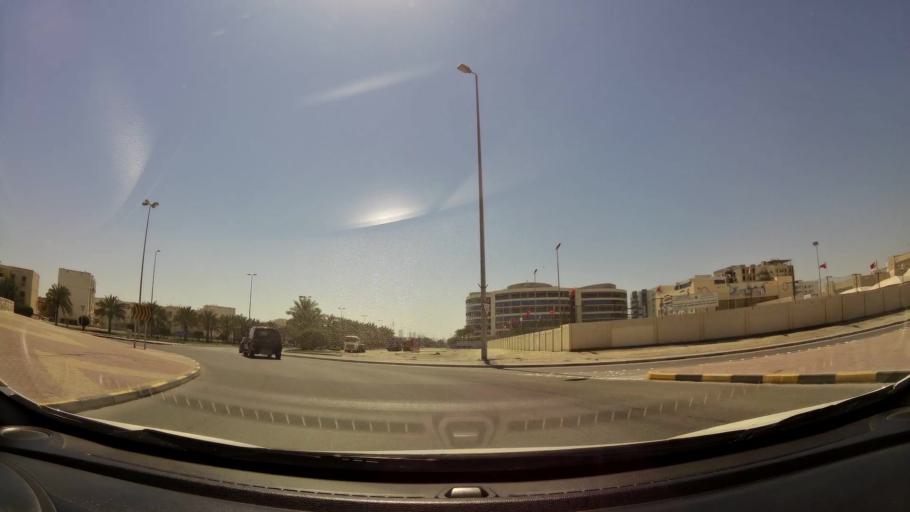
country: BH
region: Muharraq
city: Al Muharraq
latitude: 26.2667
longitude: 50.6028
